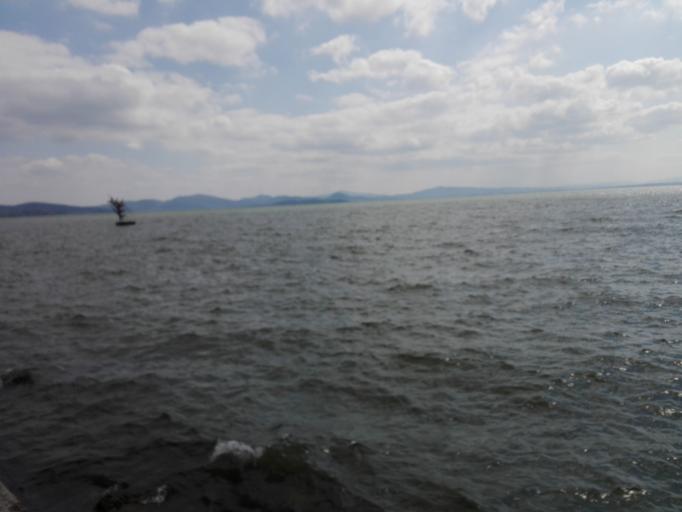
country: IT
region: Umbria
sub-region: Provincia di Perugia
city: Passignano sul Trasimeno
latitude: 43.1831
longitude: 12.1365
